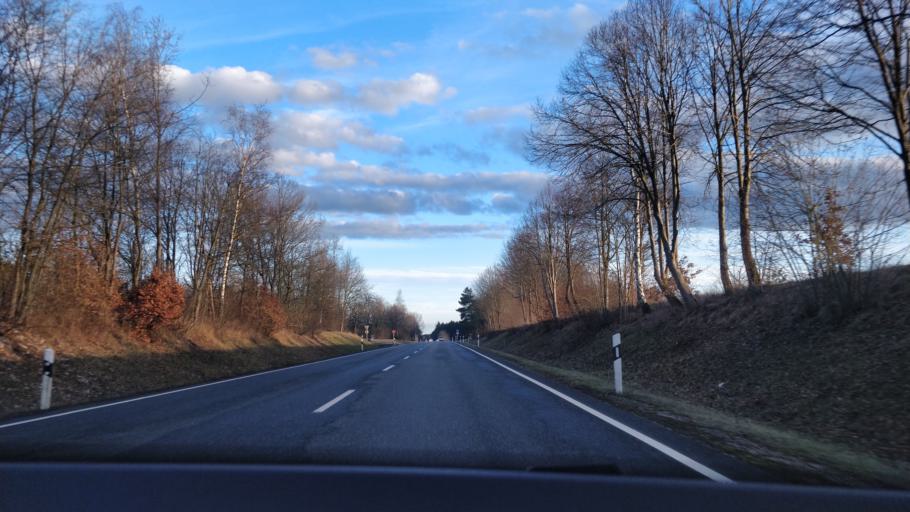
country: DE
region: Bavaria
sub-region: Upper Palatinate
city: Pressath
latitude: 49.7578
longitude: 11.9281
